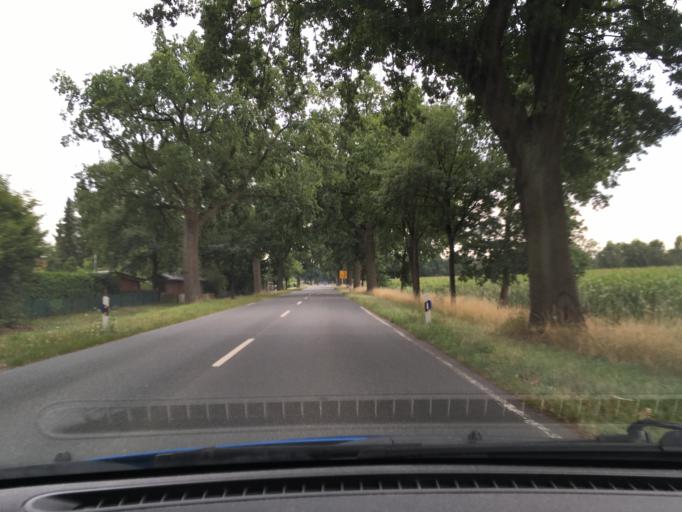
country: DE
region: Lower Saxony
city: Adelheidsdorf
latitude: 52.5491
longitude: 10.0547
